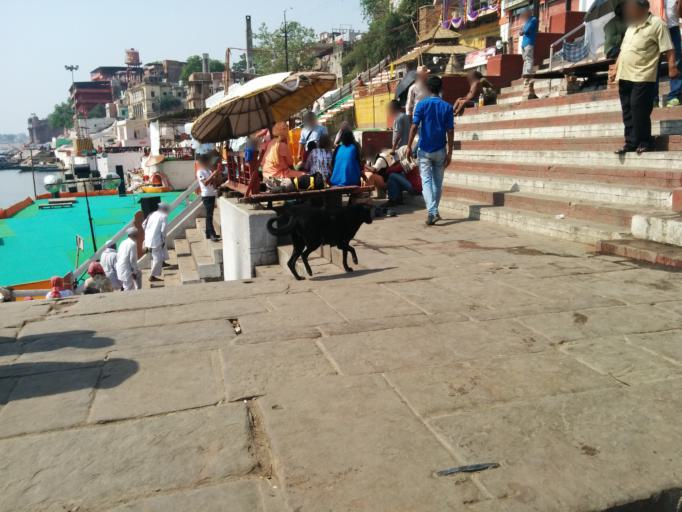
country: IN
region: Uttar Pradesh
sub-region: Varanasi
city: Varanasi
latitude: 25.2995
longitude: 83.0076
